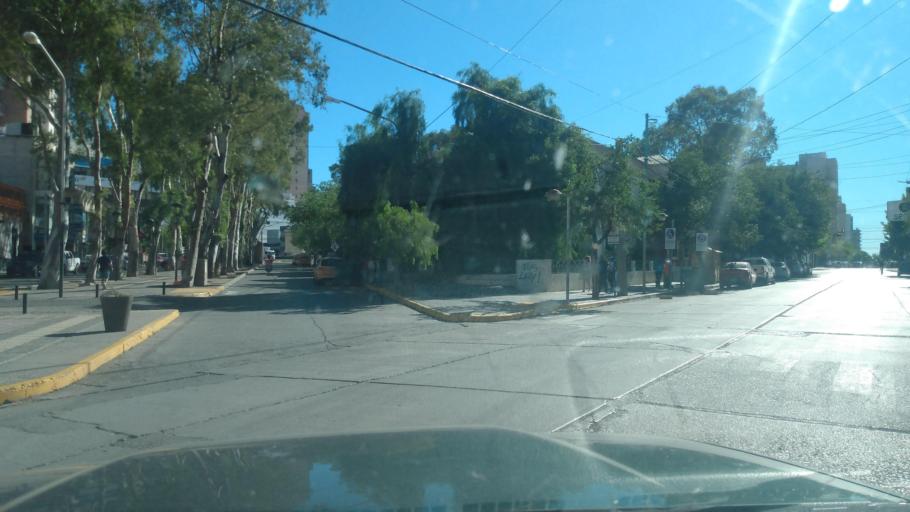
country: AR
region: Neuquen
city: Neuquen
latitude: -38.9529
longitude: -68.0606
